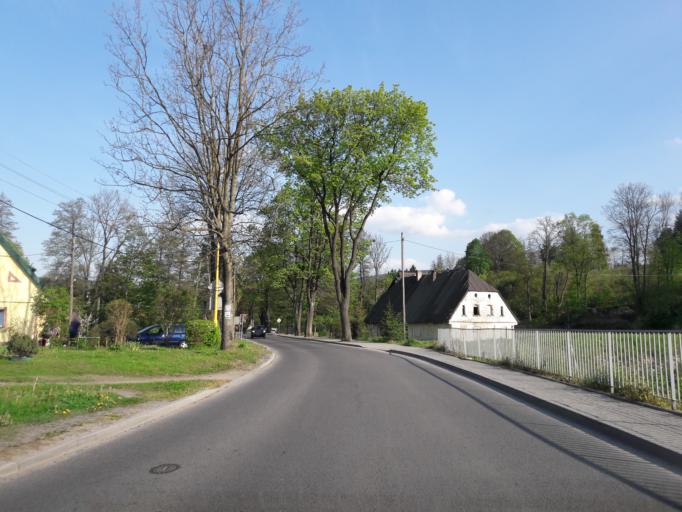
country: PL
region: Lower Silesian Voivodeship
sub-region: Powiat klodzki
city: Szczytna
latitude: 50.4193
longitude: 16.4365
